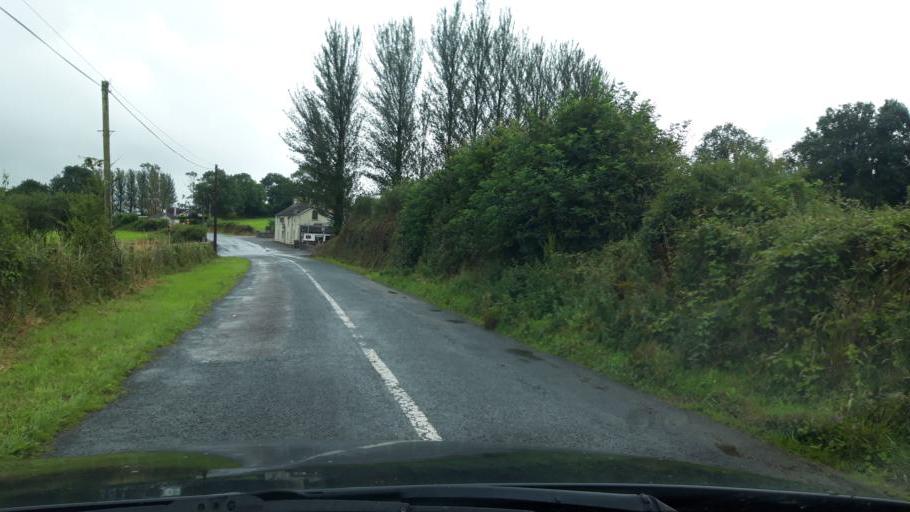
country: IE
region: Munster
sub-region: County Cork
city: Youghal
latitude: 52.1672
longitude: -7.8546
